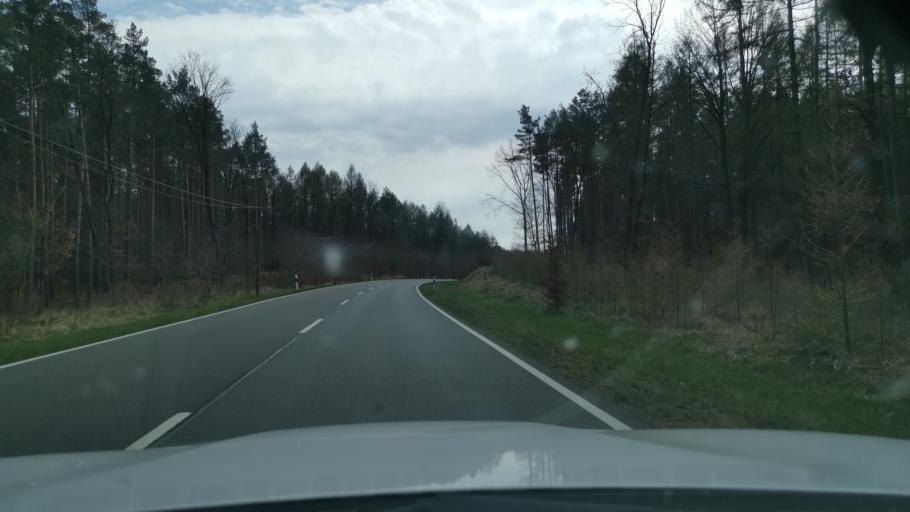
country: DE
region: Saxony-Anhalt
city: Kemberg
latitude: 51.7149
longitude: 12.6183
